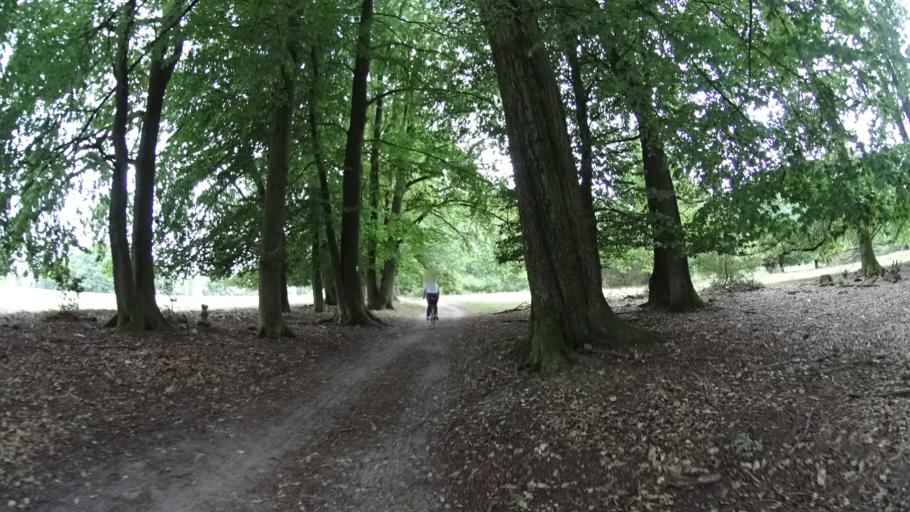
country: DE
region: Lower Saxony
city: Undeloh
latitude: 53.1583
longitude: 9.9644
